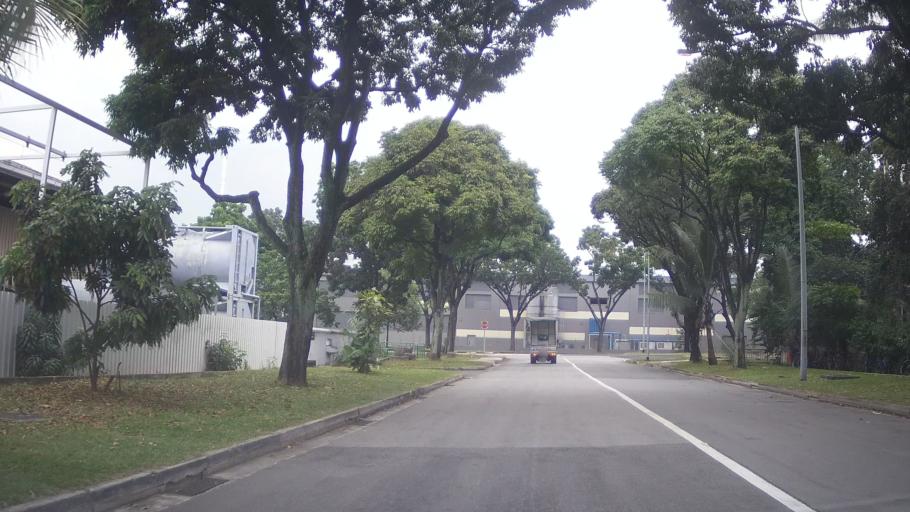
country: MY
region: Johor
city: Johor Bahru
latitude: 1.3270
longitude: 103.7059
